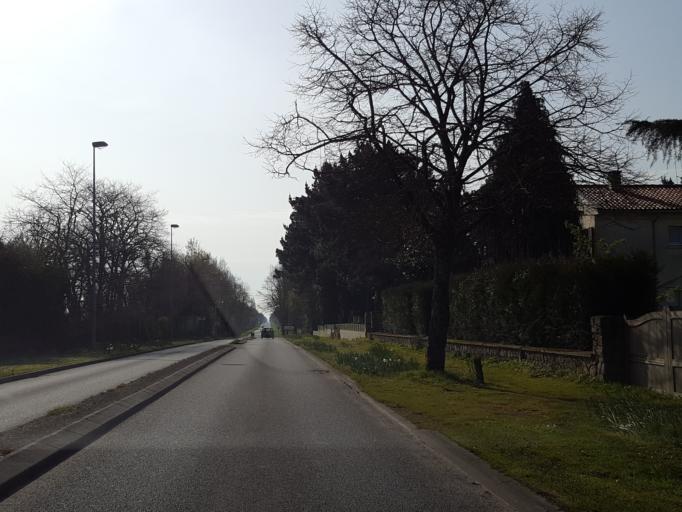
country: FR
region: Pays de la Loire
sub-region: Departement de la Vendee
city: Les Lucs-sur-Boulogne
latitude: 46.8388
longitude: -1.4896
